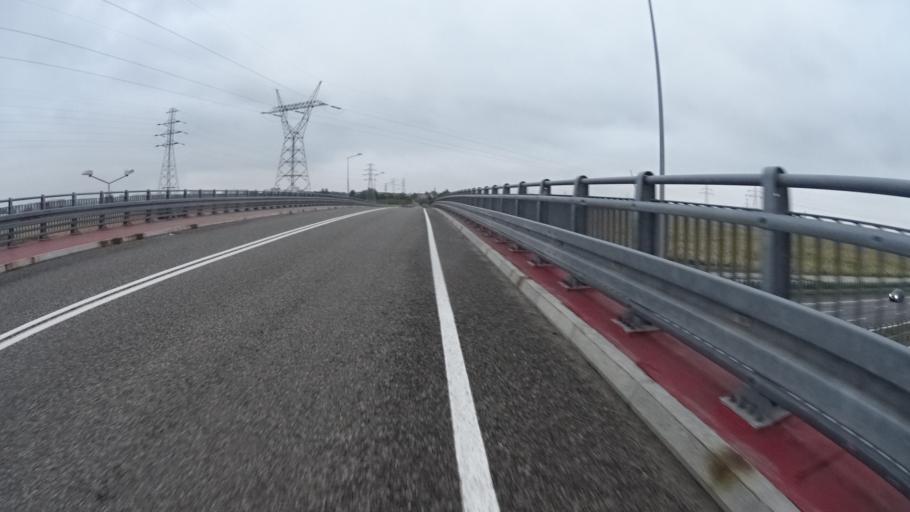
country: PL
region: Masovian Voivodeship
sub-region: Warszawa
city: Ursus
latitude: 52.2234
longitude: 20.8713
